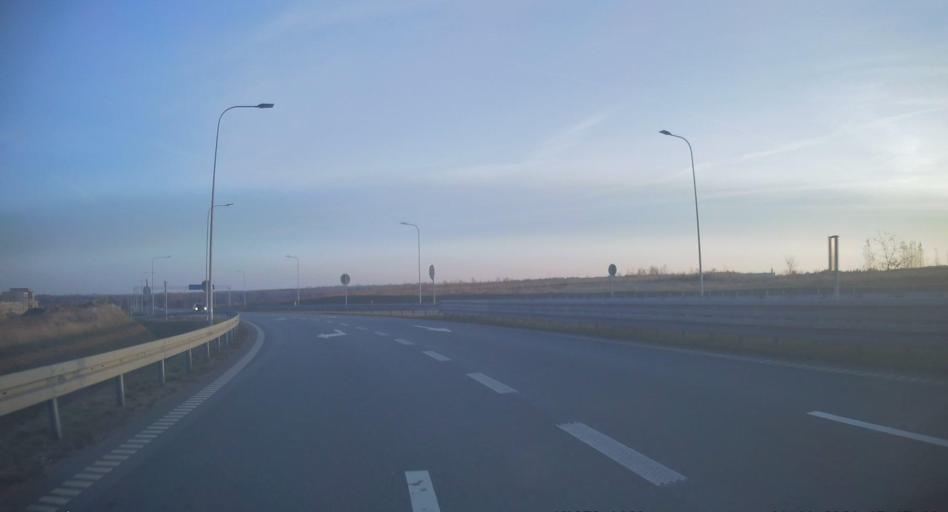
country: PL
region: Silesian Voivodeship
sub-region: Powiat klobucki
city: Kamyk
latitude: 50.8500
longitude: 19.0358
